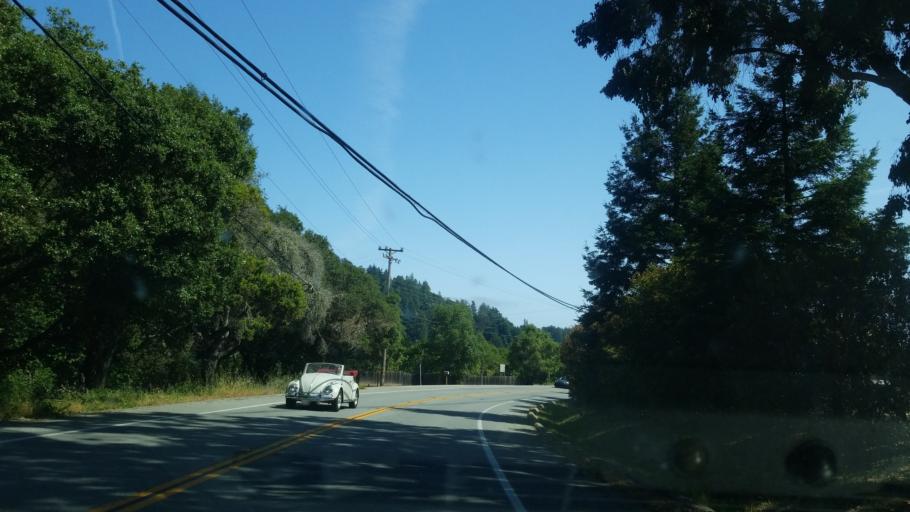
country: US
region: California
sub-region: Santa Cruz County
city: Soquel
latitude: 37.0167
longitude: -121.9521
